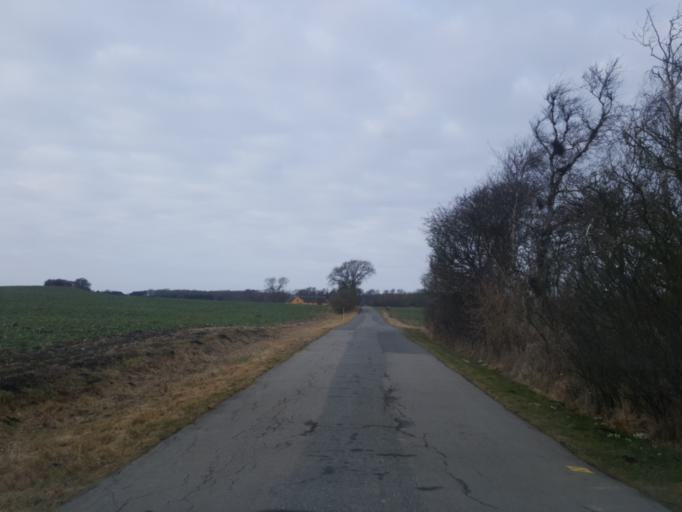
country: DK
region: Zealand
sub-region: Vordingborg Kommune
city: Neder Vindinge
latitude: 55.0526
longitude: 11.7624
